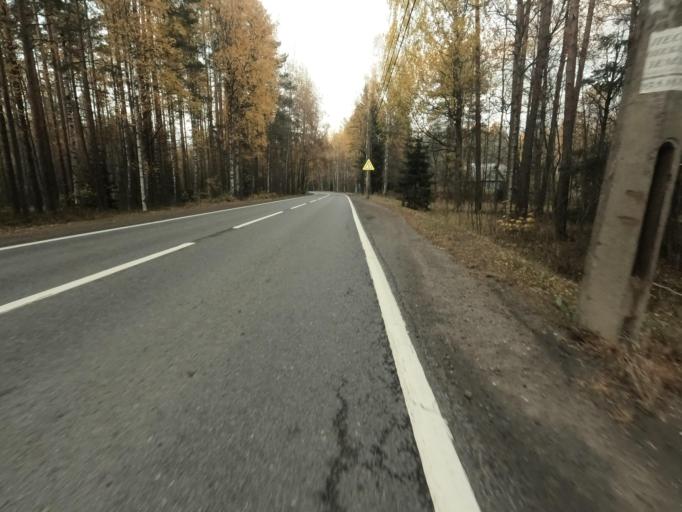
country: RU
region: St.-Petersburg
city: Repino
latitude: 60.1859
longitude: 29.8625
